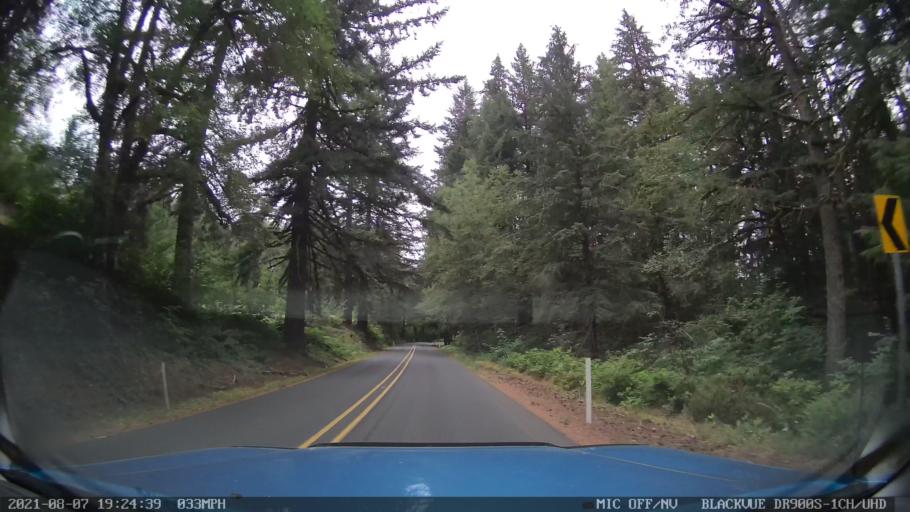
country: US
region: Oregon
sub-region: Linn County
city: Lyons
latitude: 44.8549
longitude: -122.6573
